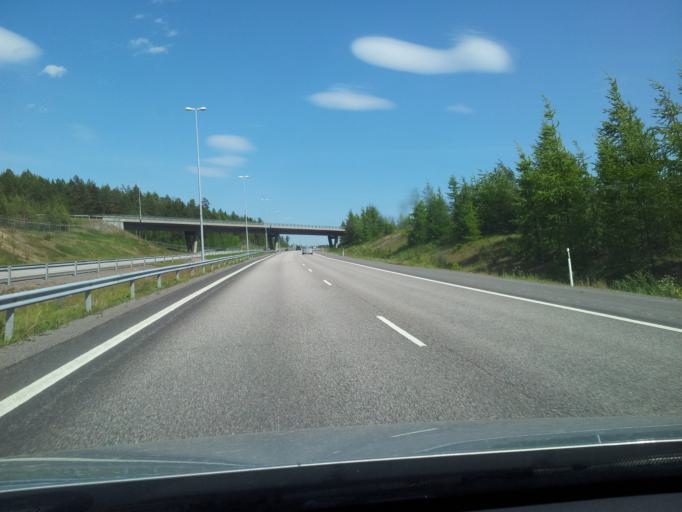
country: FI
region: Uusimaa
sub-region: Loviisa
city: Perna
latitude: 60.4916
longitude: 25.9760
